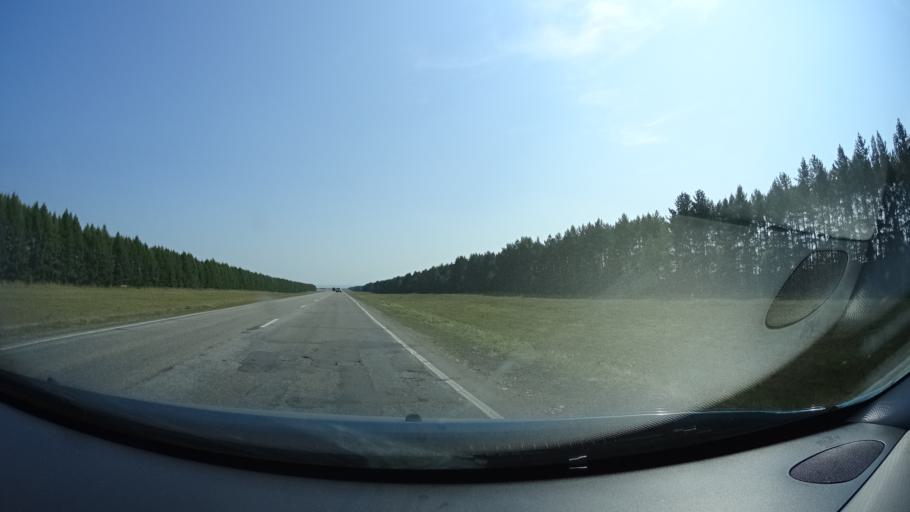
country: RU
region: Bashkortostan
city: Ulukulevo
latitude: 54.4497
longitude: 56.5325
